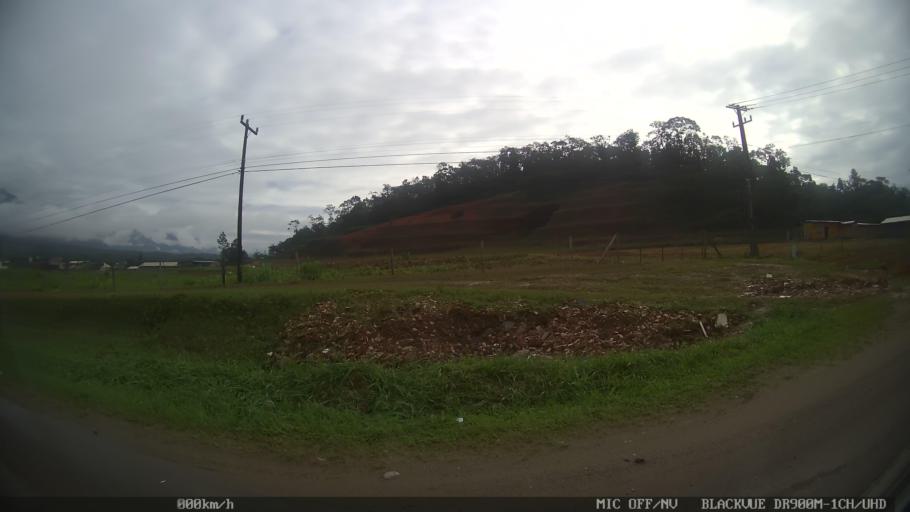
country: BR
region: Santa Catarina
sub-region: Joinville
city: Joinville
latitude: -26.0289
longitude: -48.8468
